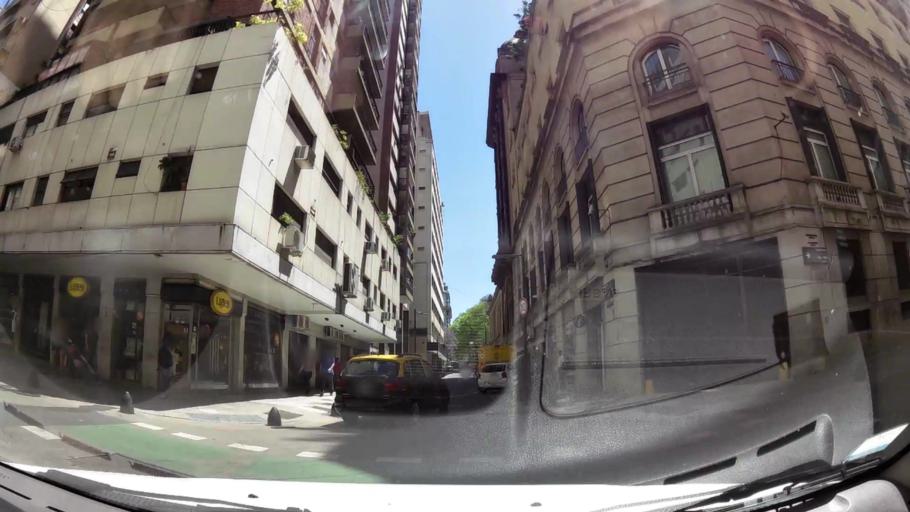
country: AR
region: Buenos Aires F.D.
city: Retiro
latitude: -34.5963
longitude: -58.3742
